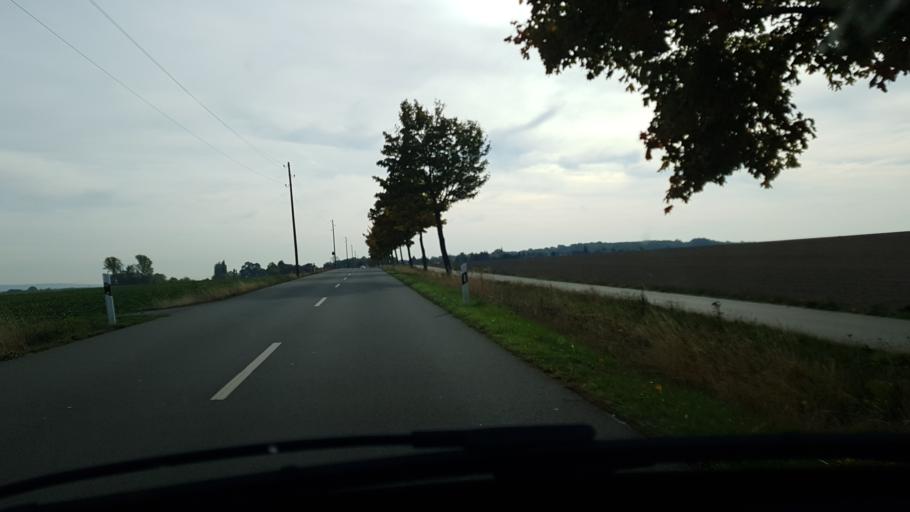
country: DE
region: Lower Saxony
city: Lehre
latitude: 52.3608
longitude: 10.6725
